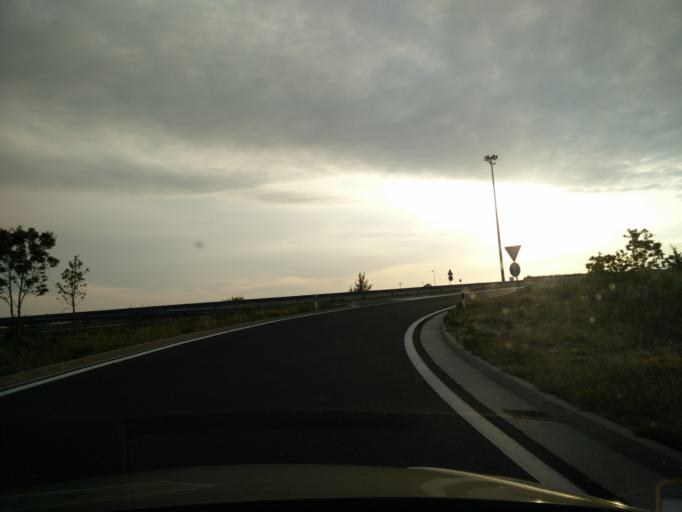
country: HR
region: Zadarska
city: Galovac
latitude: 44.1137
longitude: 15.4466
